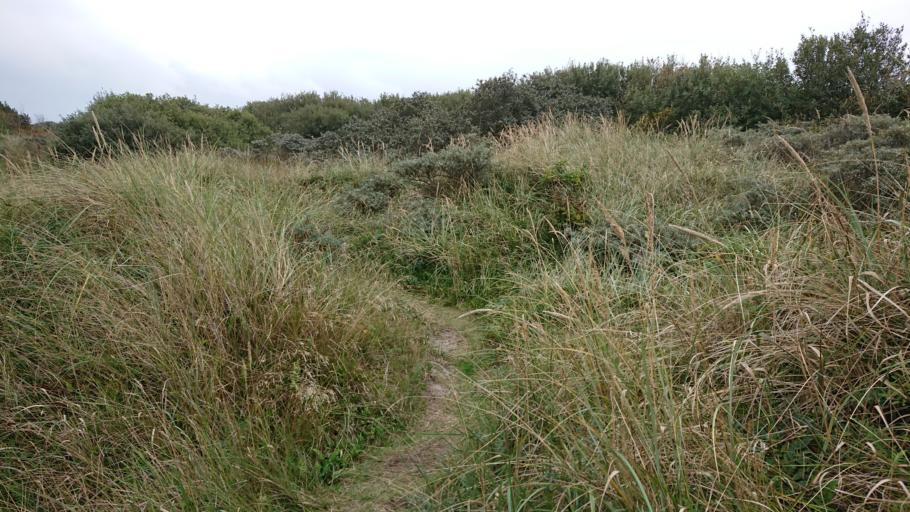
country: DK
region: North Denmark
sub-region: Frederikshavn Kommune
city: Skagen
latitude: 57.7481
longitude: 10.6192
